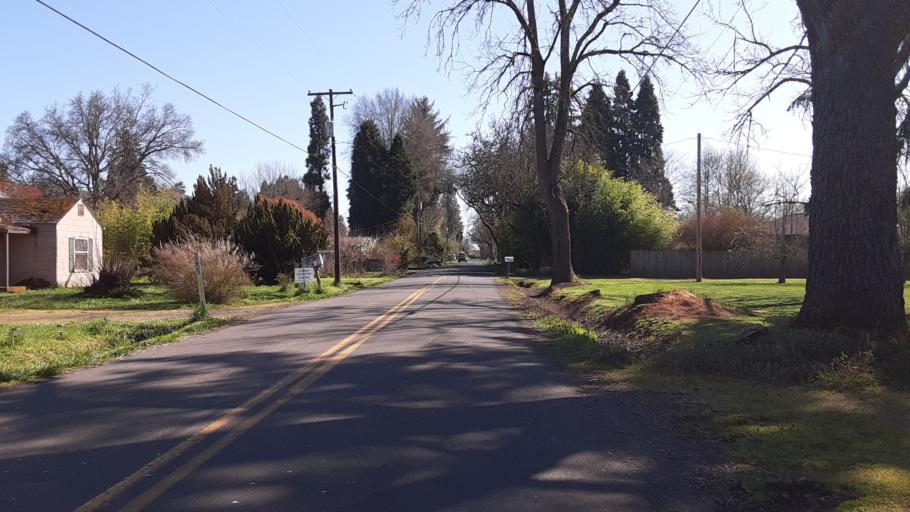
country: US
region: Oregon
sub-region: Benton County
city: Corvallis
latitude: 44.5437
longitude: -123.2556
